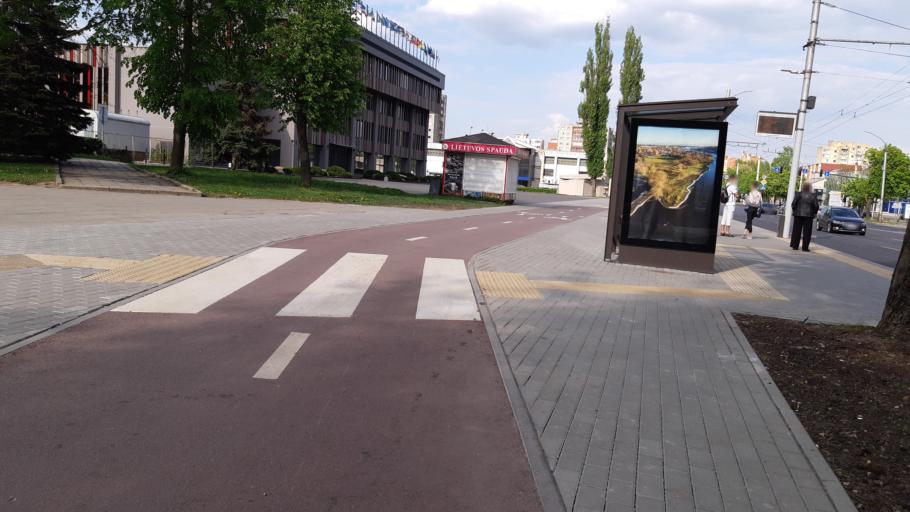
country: LT
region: Kauno apskritis
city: Dainava (Kaunas)
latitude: 54.9233
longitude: 23.9607
